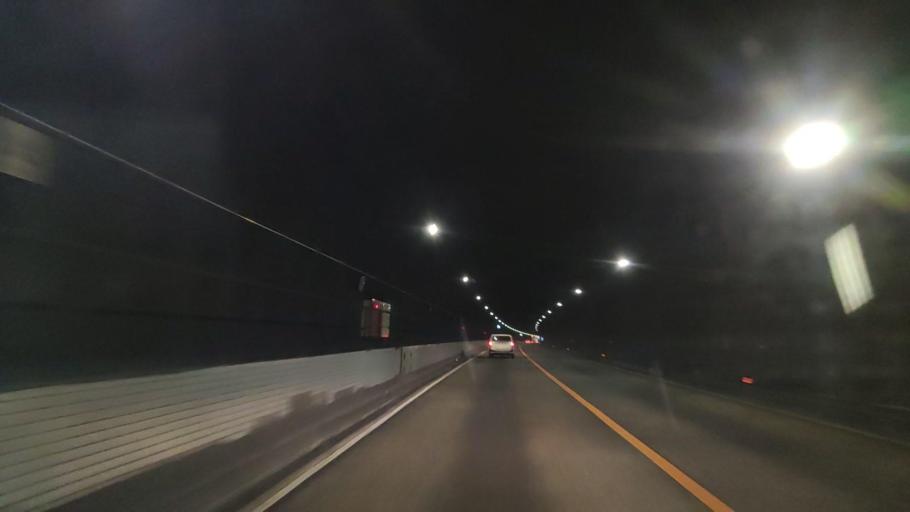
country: JP
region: Okayama
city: Okayama-shi
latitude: 34.7164
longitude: 133.9356
